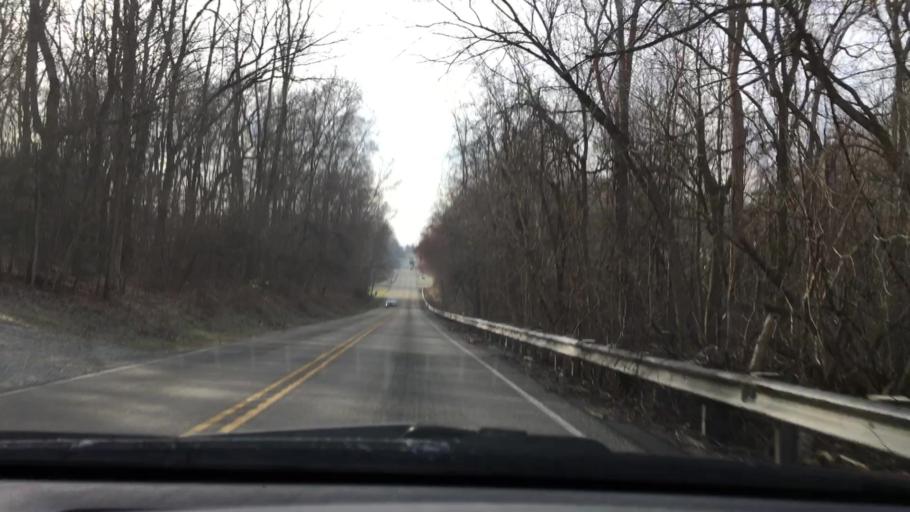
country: US
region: Pennsylvania
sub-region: Allegheny County
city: Industry
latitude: 40.2641
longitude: -79.7680
